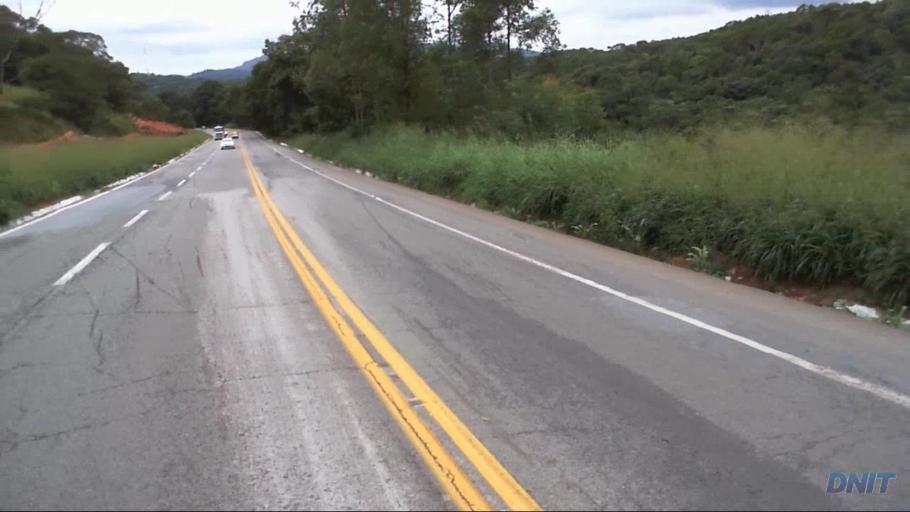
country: BR
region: Minas Gerais
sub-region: Barao De Cocais
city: Barao de Cocais
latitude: -19.7979
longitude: -43.4162
